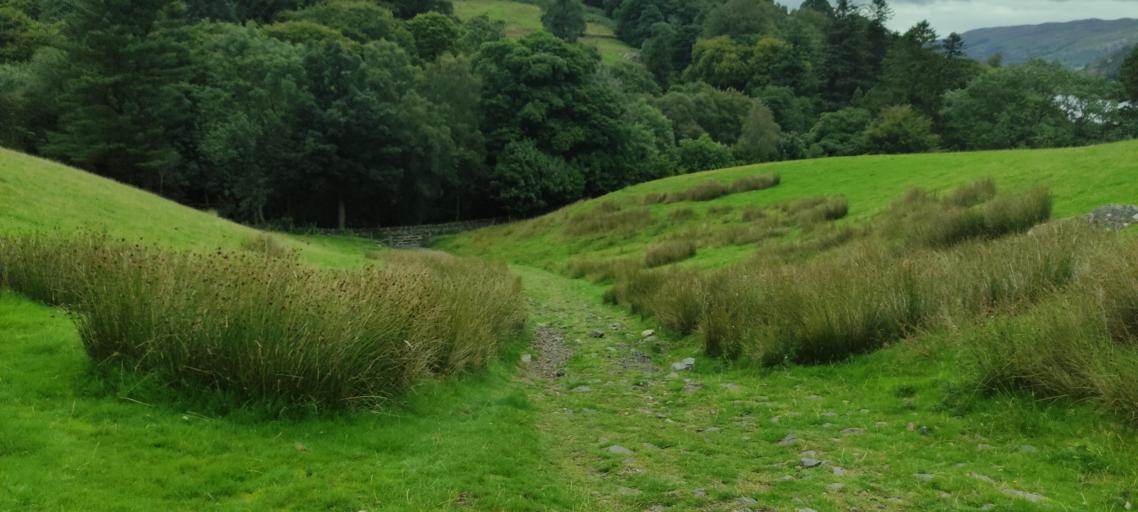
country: GB
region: England
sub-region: Cumbria
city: Ambleside
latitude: 54.5331
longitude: -2.9490
